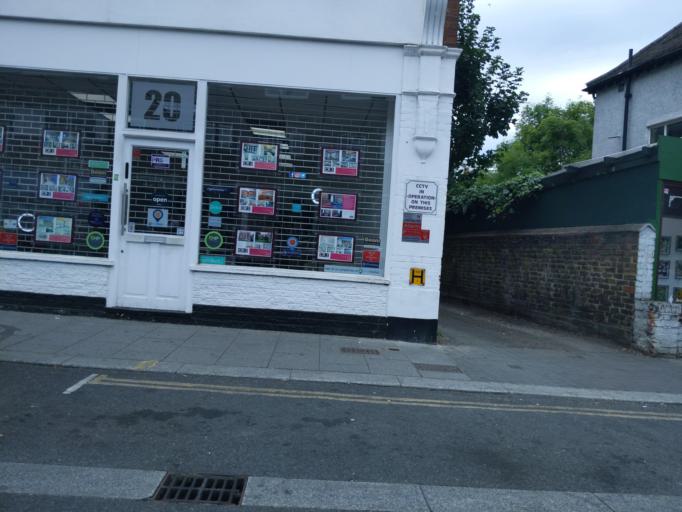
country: GB
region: England
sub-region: Greater London
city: South Croydon
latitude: 51.3630
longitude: -0.0972
